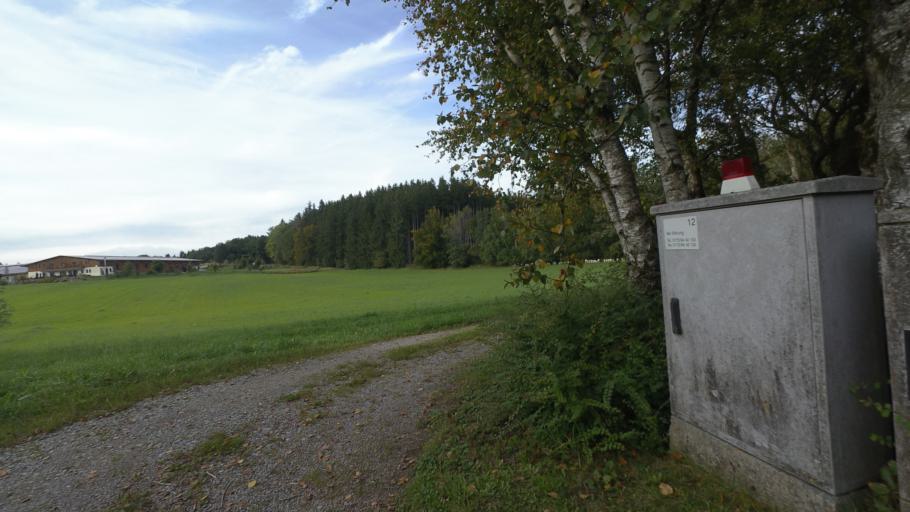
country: DE
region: Bavaria
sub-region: Upper Bavaria
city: Chieming
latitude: 47.9295
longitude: 12.5464
